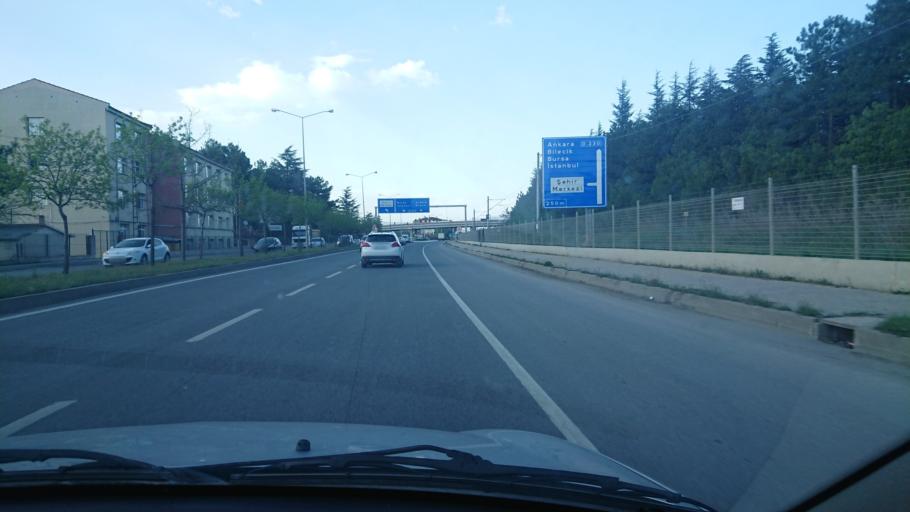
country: TR
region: Eskisehir
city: Eskisehir
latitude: 39.7661
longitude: 30.4796
